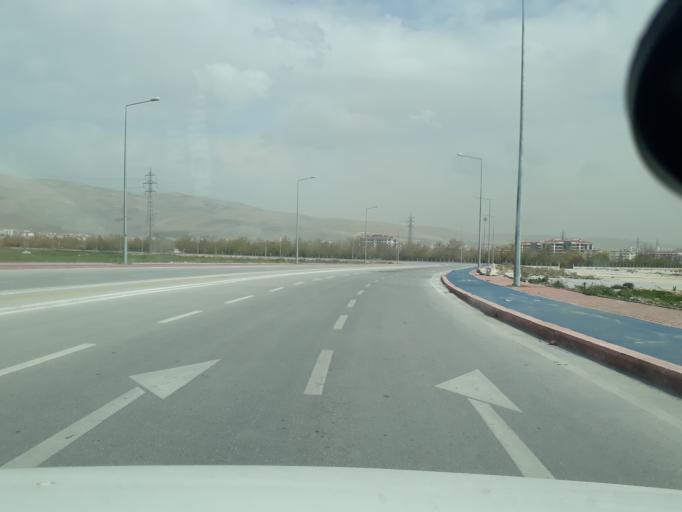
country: TR
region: Konya
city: Selcuklu
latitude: 37.9442
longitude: 32.4805
